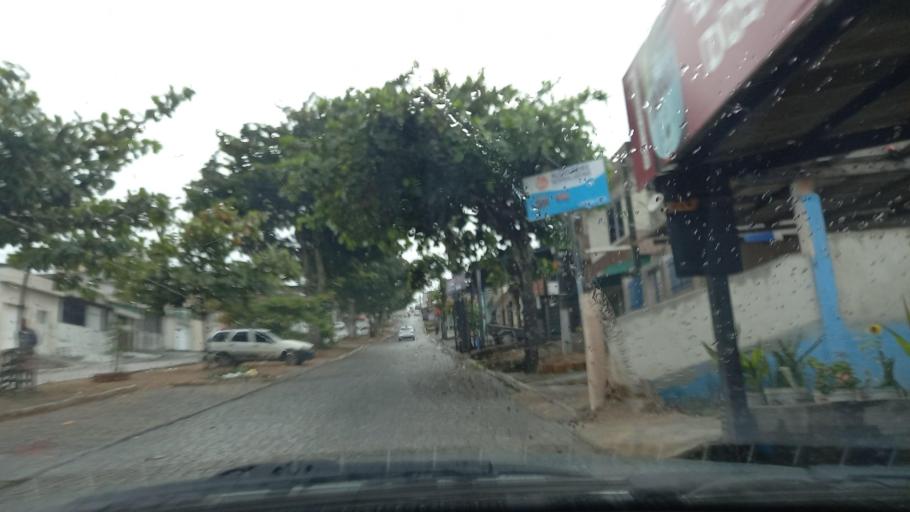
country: BR
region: Pernambuco
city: Garanhuns
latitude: -8.8839
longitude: -36.5005
